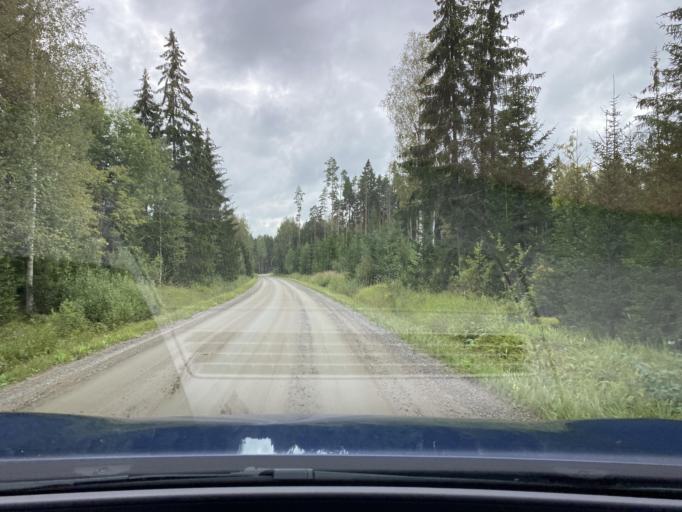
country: FI
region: Pirkanmaa
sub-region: Lounais-Pirkanmaa
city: Punkalaidun
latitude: 61.1992
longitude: 23.1790
